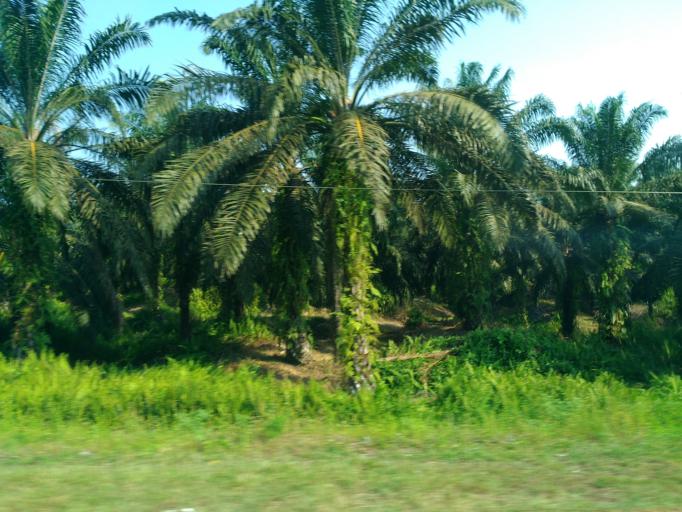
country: MY
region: Sabah
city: Taman Rajawali
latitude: 5.6950
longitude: 117.3969
